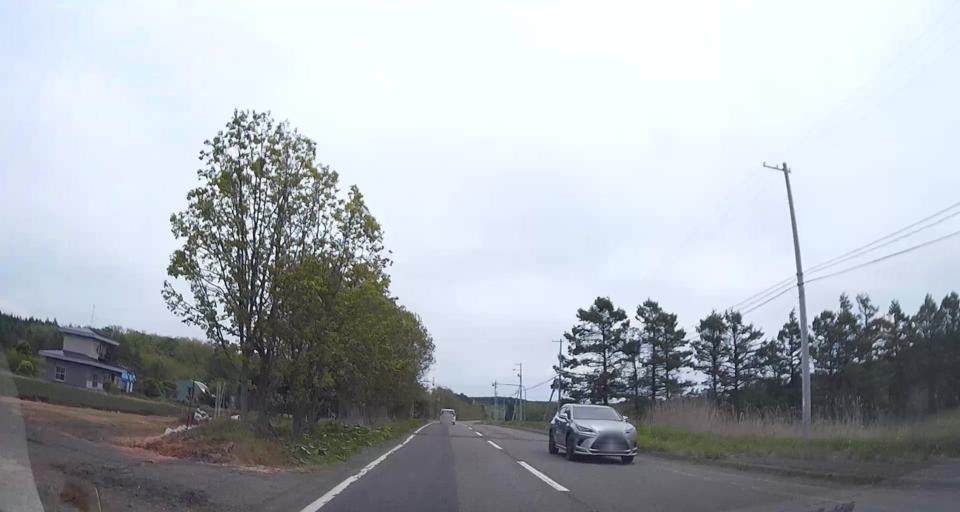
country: JP
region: Hokkaido
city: Chitose
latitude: 42.7724
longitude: 141.8360
